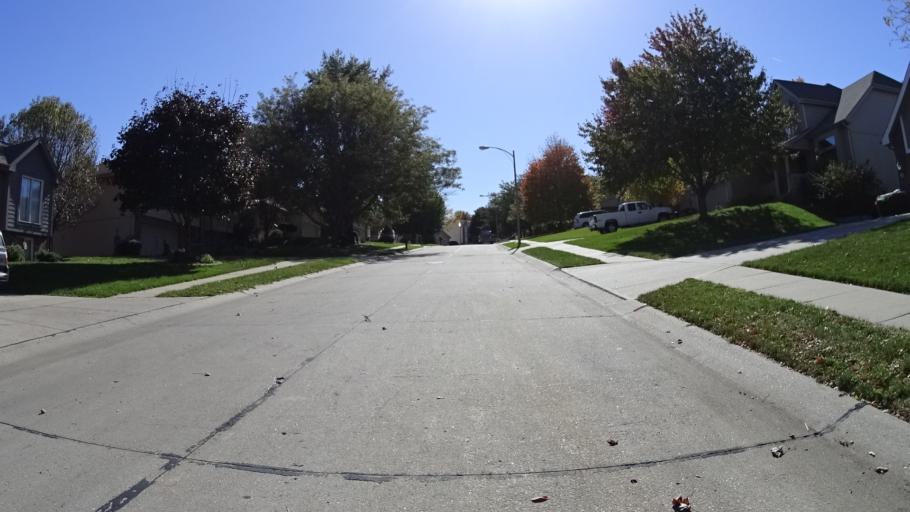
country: US
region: Nebraska
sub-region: Sarpy County
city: La Vista
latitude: 41.1671
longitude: -96.0245
